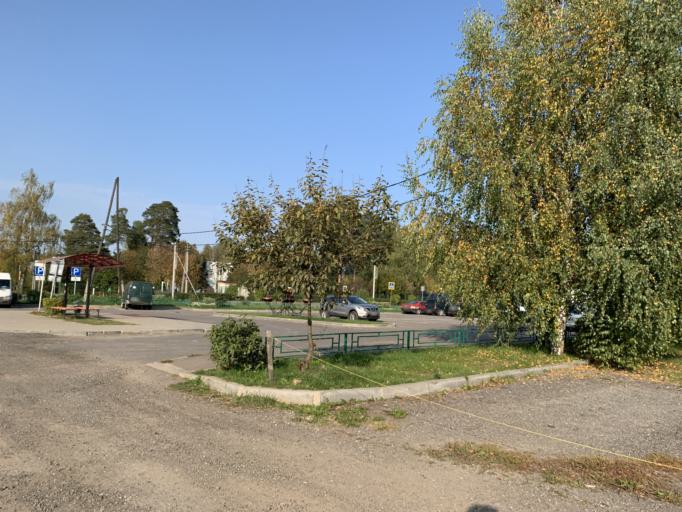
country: RU
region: Moskovskaya
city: Lesnyye Polyany
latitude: 55.9638
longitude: 37.8467
